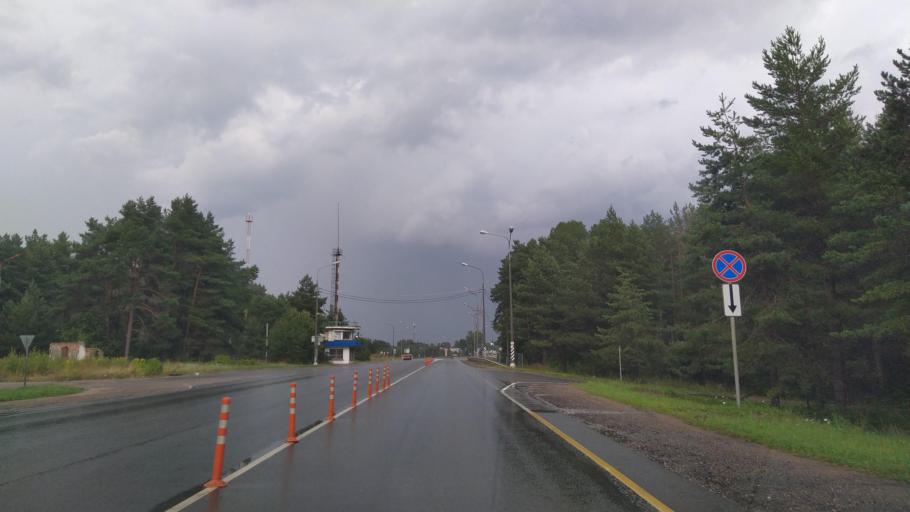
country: RU
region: Pskov
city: Pskov
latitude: 57.7388
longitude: 28.3648
